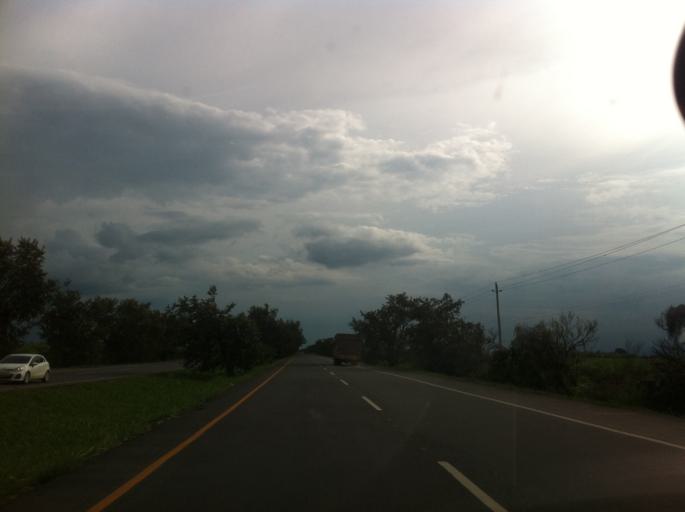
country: CO
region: Valle del Cauca
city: Palmira
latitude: 3.5617
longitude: -76.3347
